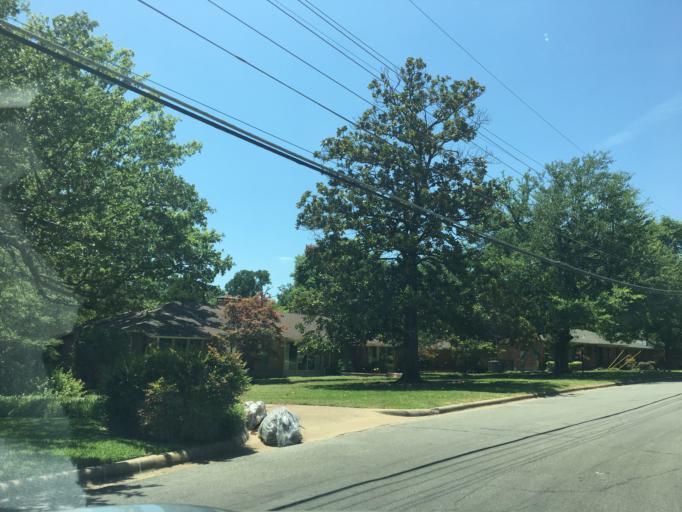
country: US
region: Texas
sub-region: Dallas County
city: Highland Park
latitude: 32.8433
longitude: -96.7357
